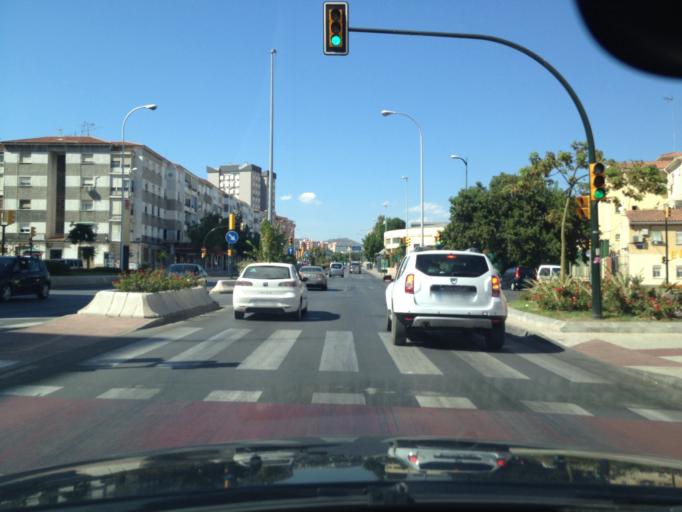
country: ES
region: Andalusia
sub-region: Provincia de Malaga
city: Malaga
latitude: 36.7110
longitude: -4.4456
